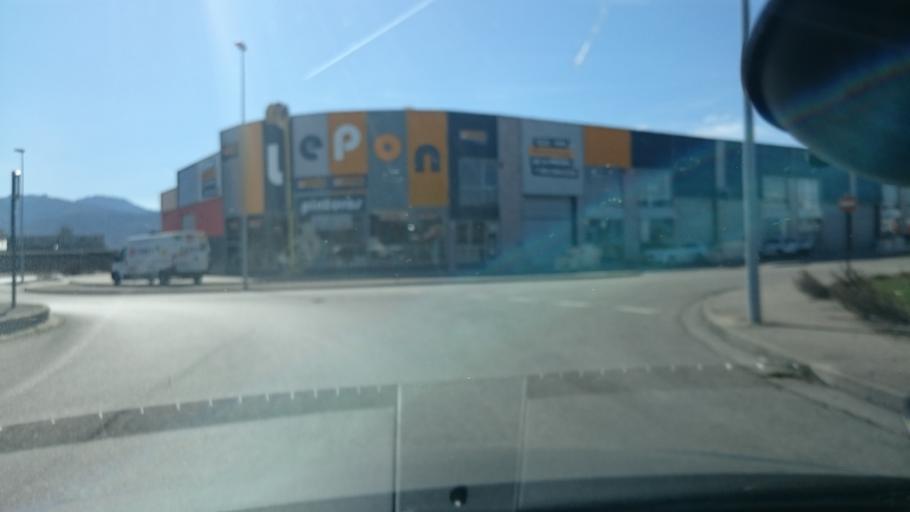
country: ES
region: Castille and Leon
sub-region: Provincia de Leon
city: Ponferrada
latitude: 42.5519
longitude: -6.6164
